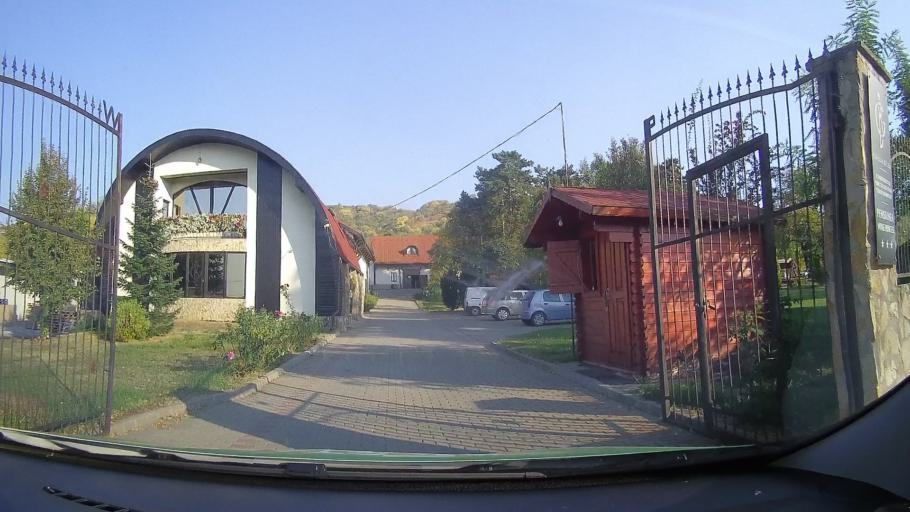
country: RO
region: Arad
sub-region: Comuna Paulis
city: Paulis
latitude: 46.1244
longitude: 21.5992
